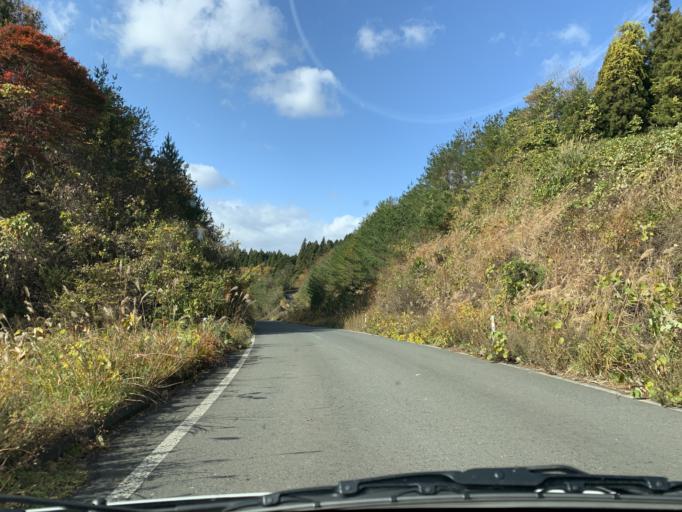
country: JP
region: Iwate
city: Mizusawa
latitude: 39.0350
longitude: 141.0811
